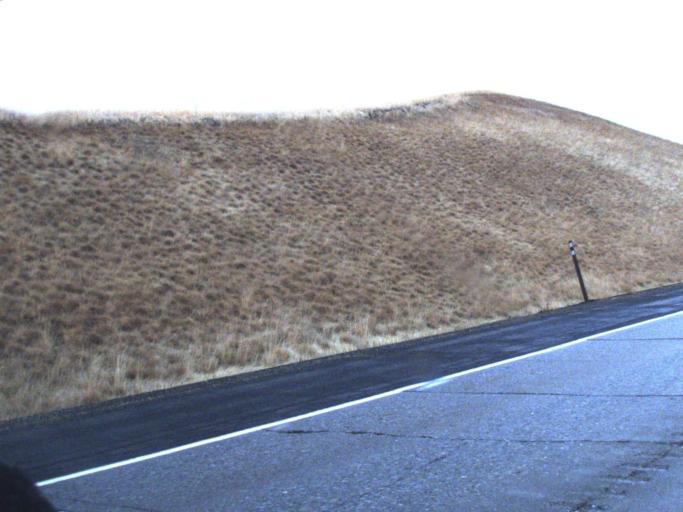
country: US
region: Washington
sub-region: Whitman County
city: Colfax
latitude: 47.1407
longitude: -117.3795
